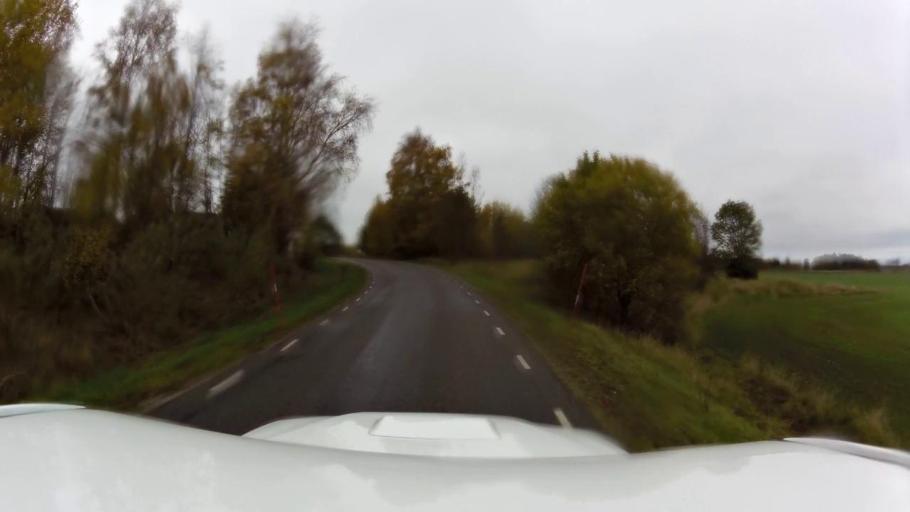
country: SE
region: OEstergoetland
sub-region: Linkopings Kommun
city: Linghem
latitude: 58.4752
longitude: 15.7232
